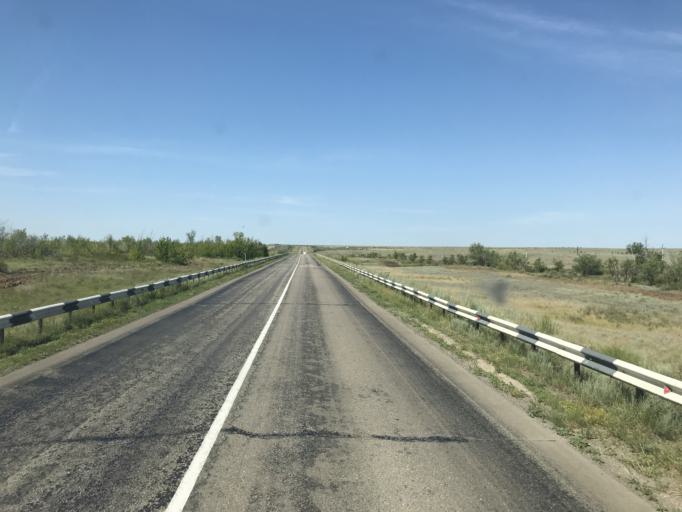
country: KZ
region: Aqtoebe
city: Martuk
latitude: 50.2346
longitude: 56.6645
